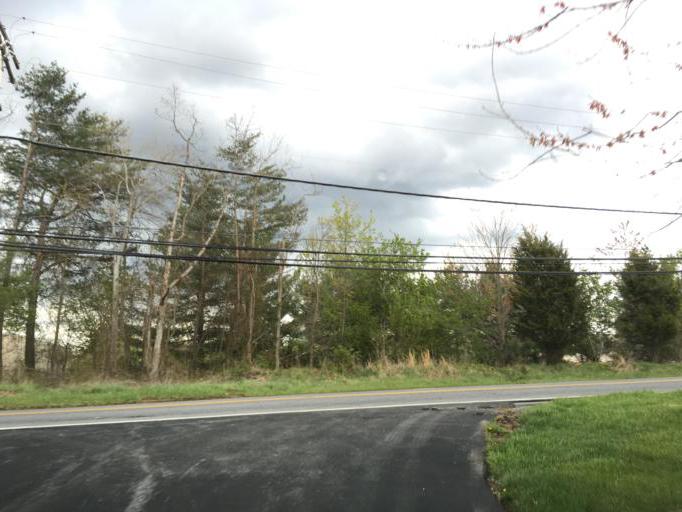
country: US
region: Maryland
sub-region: Howard County
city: Hanover
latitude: 39.1731
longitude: -76.7102
